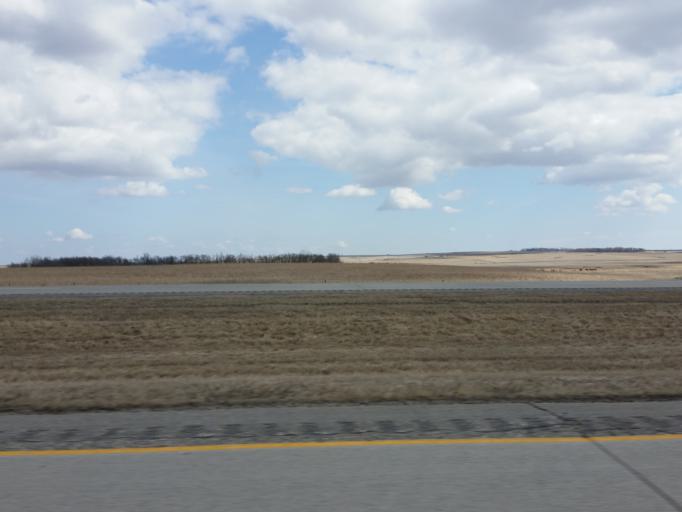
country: US
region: South Dakota
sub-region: Codington County
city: Watertown
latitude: 45.2347
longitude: -97.0515
